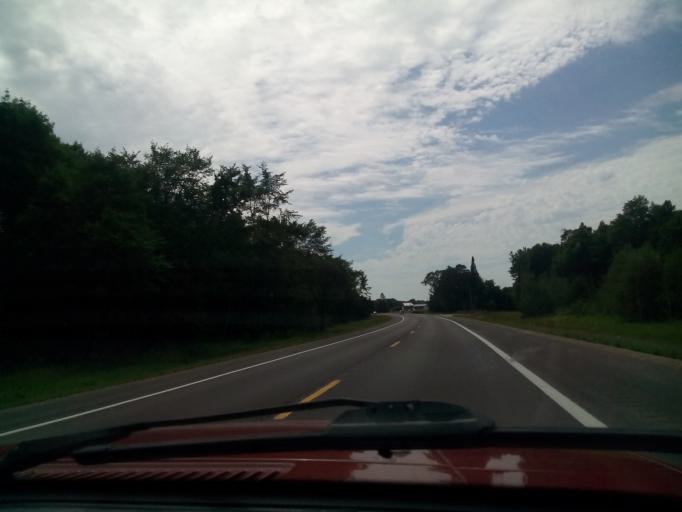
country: US
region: Michigan
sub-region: Schoolcraft County
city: Manistique
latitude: 46.0820
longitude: -85.9572
